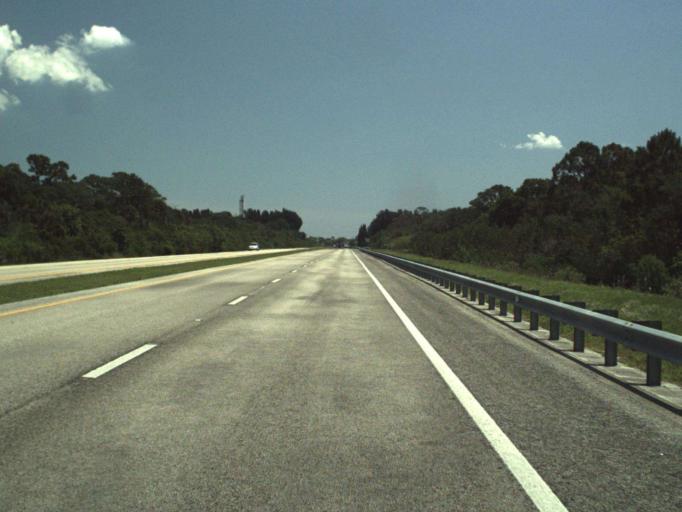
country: US
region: Florida
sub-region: Brevard County
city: Merritt Island
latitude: 28.4772
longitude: -80.6948
